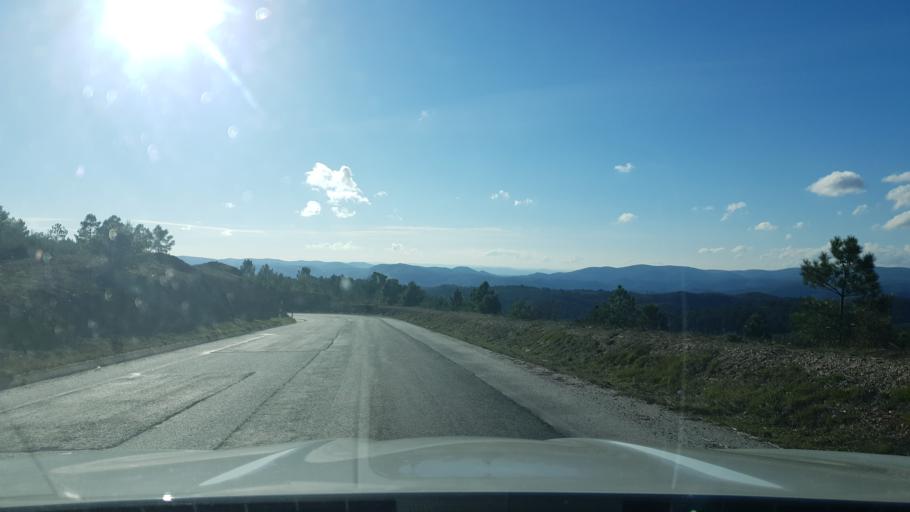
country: PT
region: Braganca
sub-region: Freixo de Espada A Cinta
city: Freixo de Espada a Cinta
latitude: 41.1303
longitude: -6.8177
